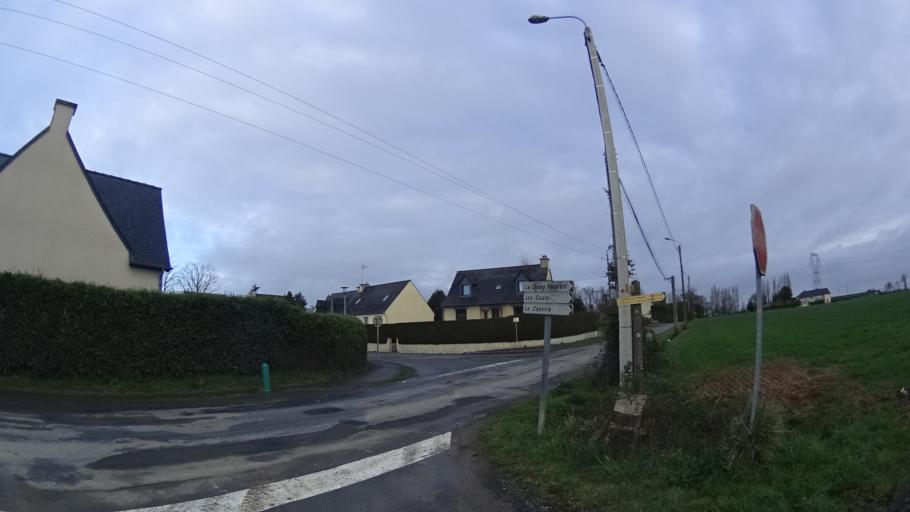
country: FR
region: Brittany
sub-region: Departement d'Ille-et-Vilaine
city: Romille
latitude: 48.2229
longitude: -1.8924
